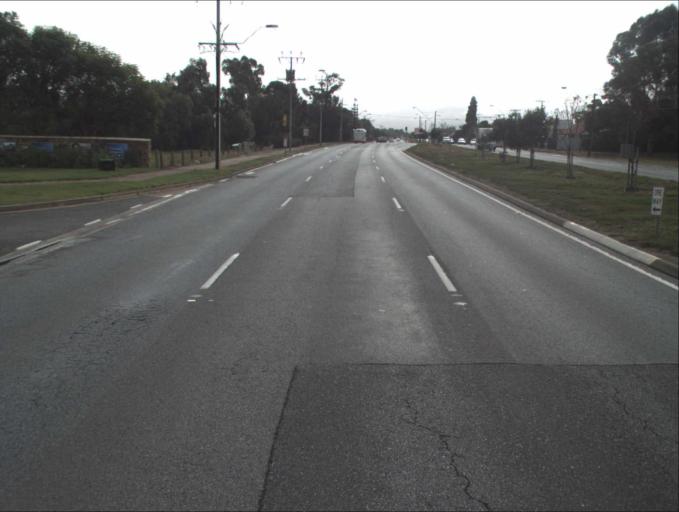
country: AU
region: South Australia
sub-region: Port Adelaide Enfield
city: Enfield
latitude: -34.8339
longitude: 138.6104
